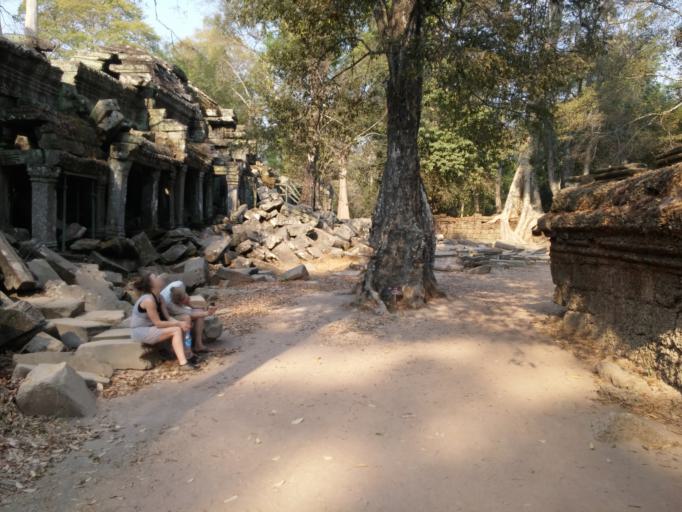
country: KH
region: Siem Reap
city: Siem Reap
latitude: 13.4354
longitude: 103.8896
